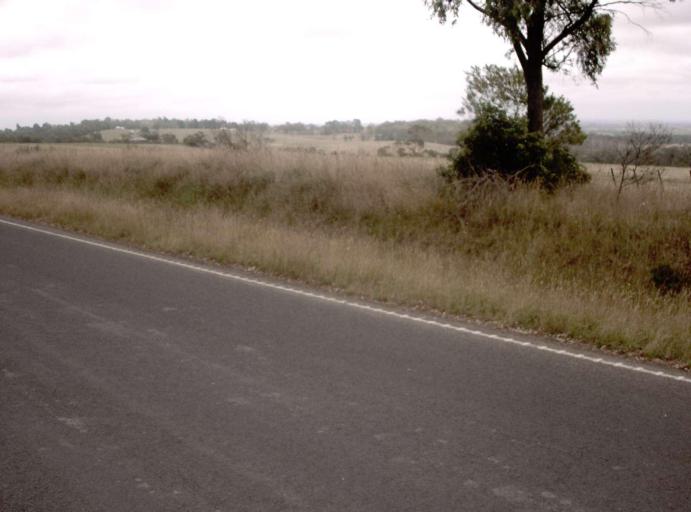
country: AU
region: Victoria
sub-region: Cardinia
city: Bunyip
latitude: -38.2288
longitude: 145.7462
